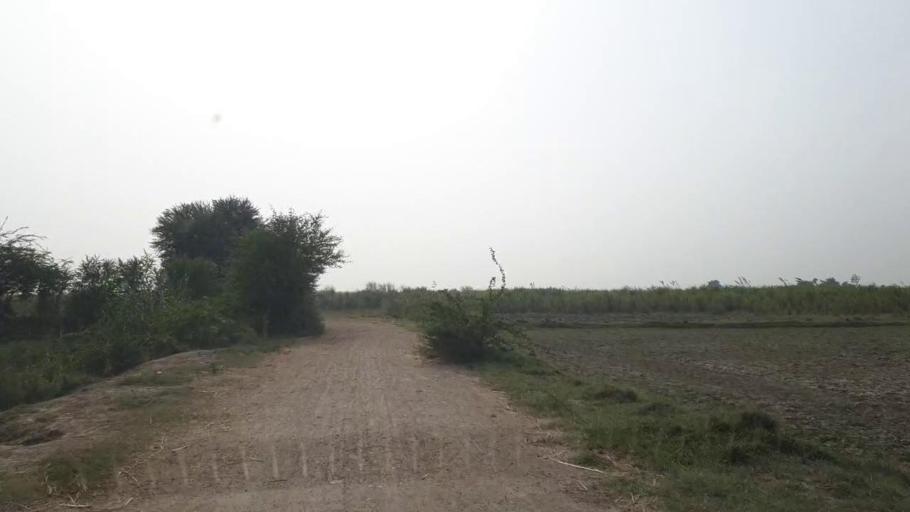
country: PK
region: Sindh
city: Matli
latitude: 25.0320
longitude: 68.5880
